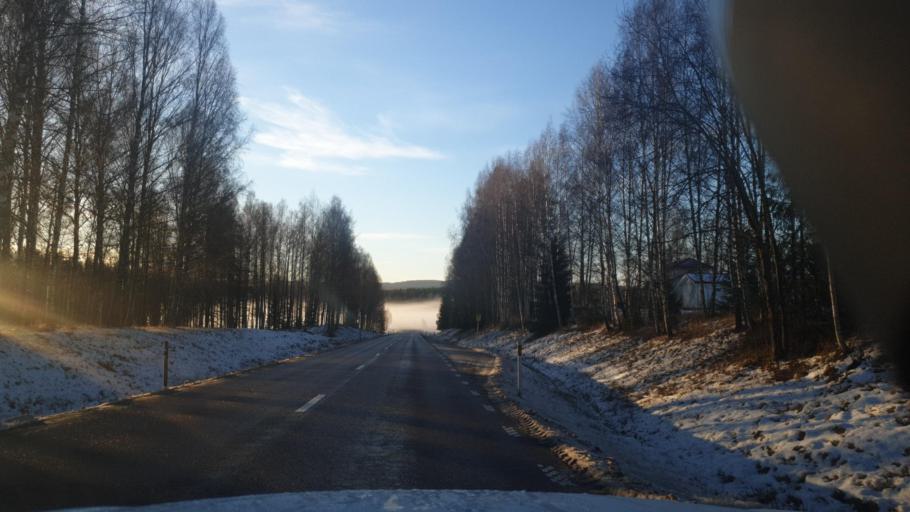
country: SE
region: Vaermland
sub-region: Arvika Kommun
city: Arvika
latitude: 59.4999
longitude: 12.7659
